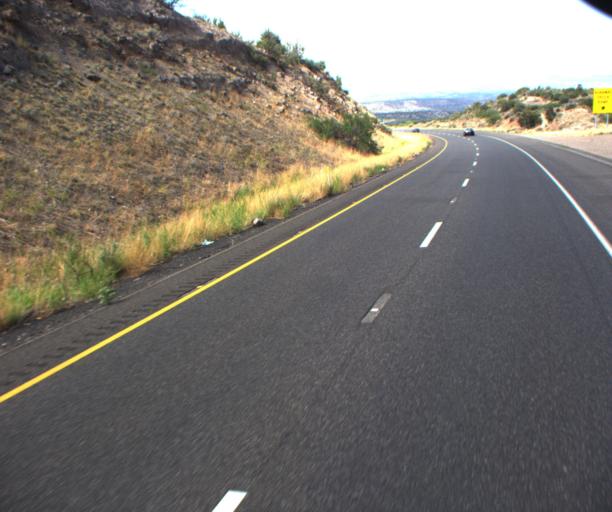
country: US
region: Arizona
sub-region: Yavapai County
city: Big Park
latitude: 34.7091
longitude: -111.7392
